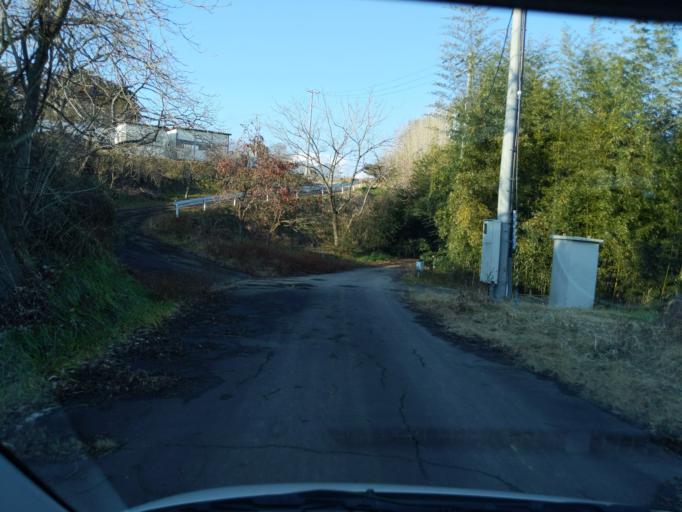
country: JP
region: Miyagi
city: Wakuya
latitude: 38.6951
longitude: 141.1240
